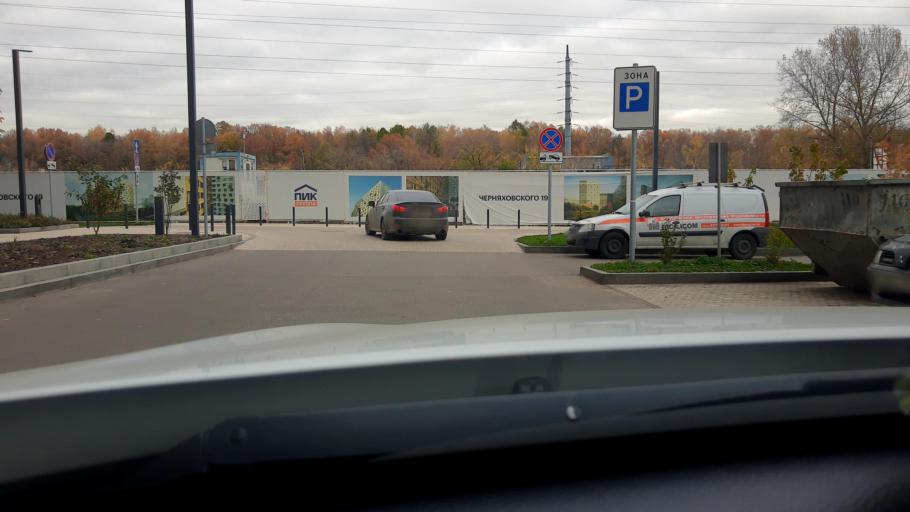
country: RU
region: Moskovskaya
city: Koptevo
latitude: 55.8085
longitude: 37.5420
